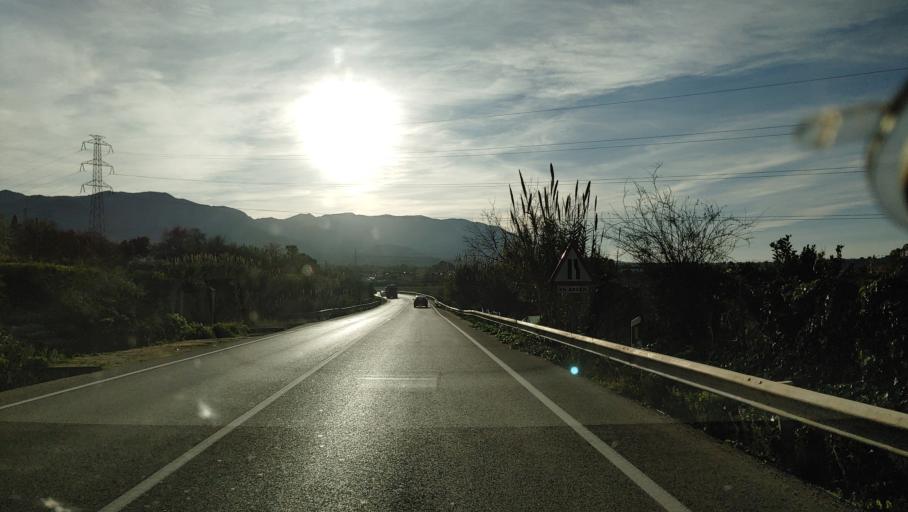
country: ES
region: Andalusia
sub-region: Provincia de Malaga
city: Alhaurin de la Torre
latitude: 36.6677
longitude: -4.5781
